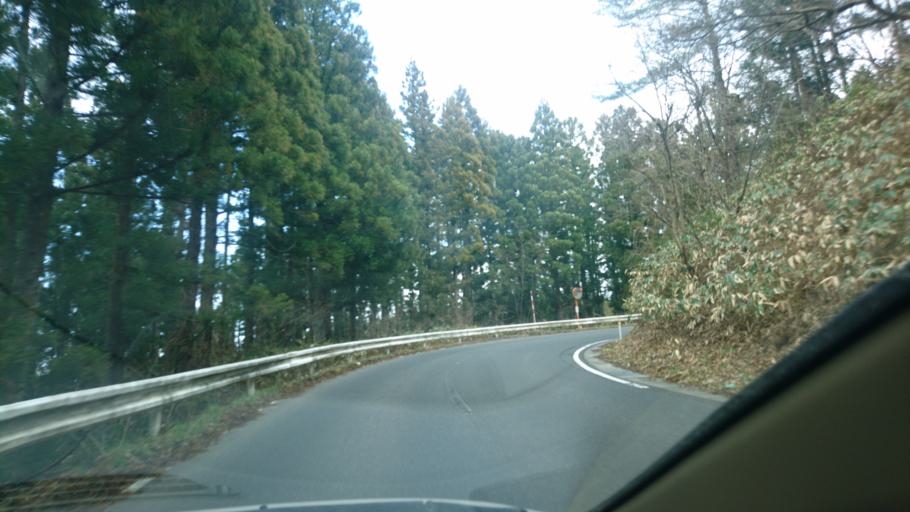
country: JP
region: Miyagi
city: Furukawa
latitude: 38.7359
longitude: 140.8475
